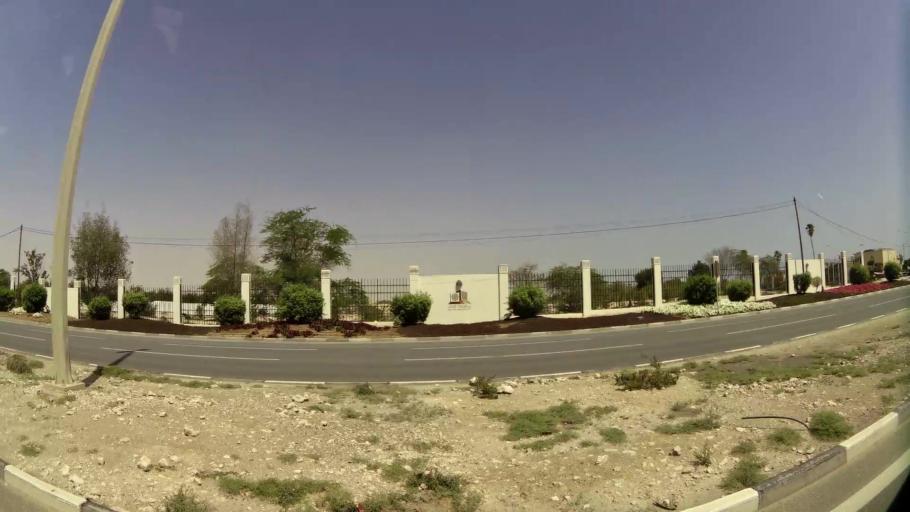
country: QA
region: Baladiyat ad Dawhah
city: Doha
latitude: 25.3580
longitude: 51.4939
